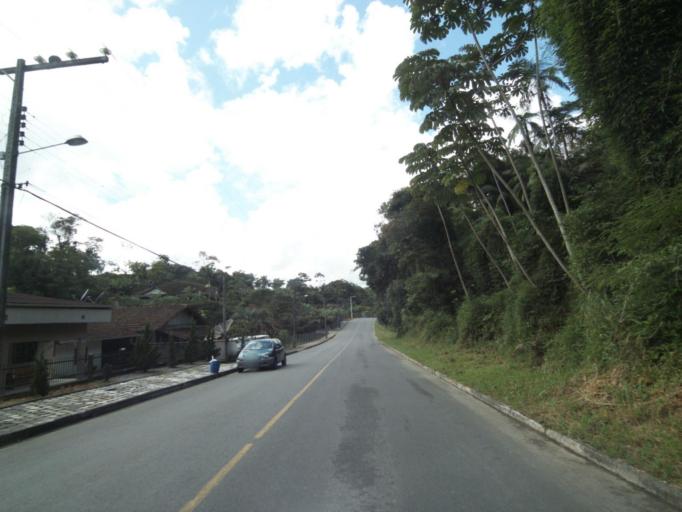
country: BR
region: Santa Catarina
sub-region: Pomerode
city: Pomerode
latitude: -26.6878
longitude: -49.1661
